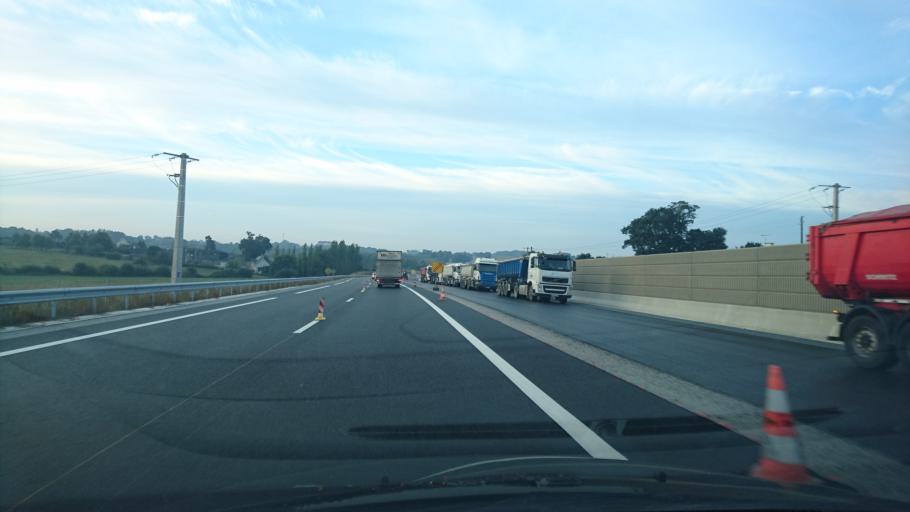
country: FR
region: Brittany
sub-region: Departement d'Ille-et-Vilaine
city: Pipriac
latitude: 47.7997
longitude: -1.9221
